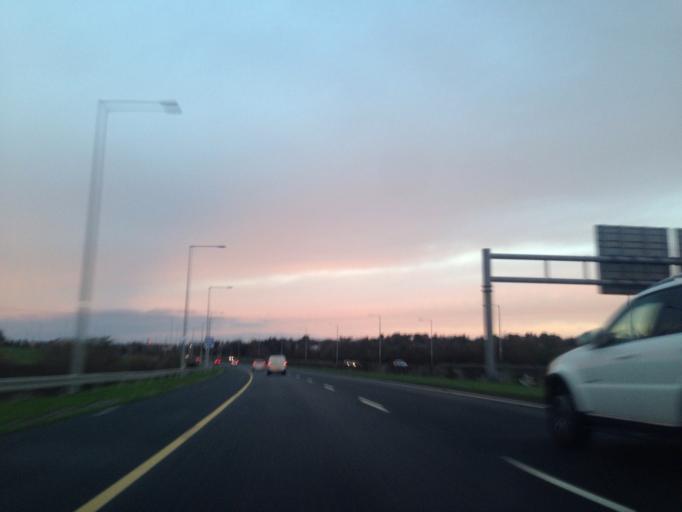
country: IE
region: Leinster
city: Foxrock
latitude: 53.2483
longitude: -6.1658
